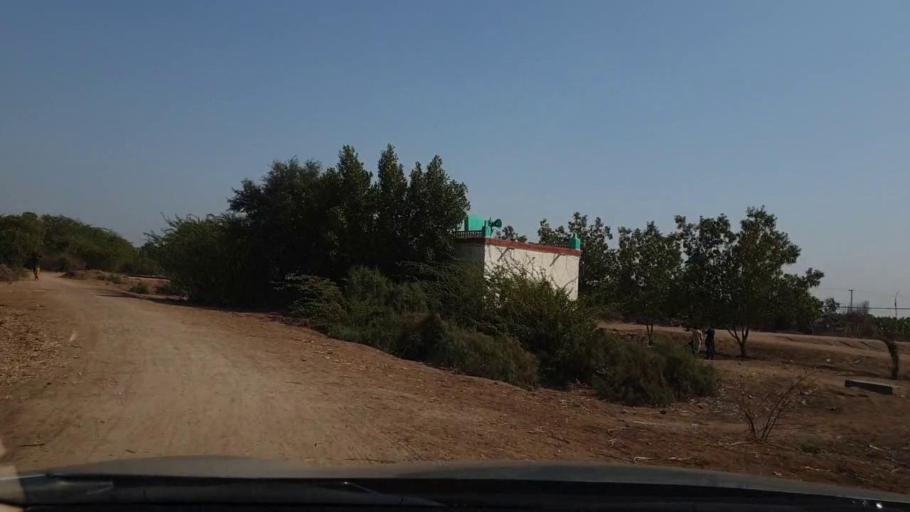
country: PK
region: Sindh
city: Mirpur Khas
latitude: 25.5905
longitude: 68.8674
